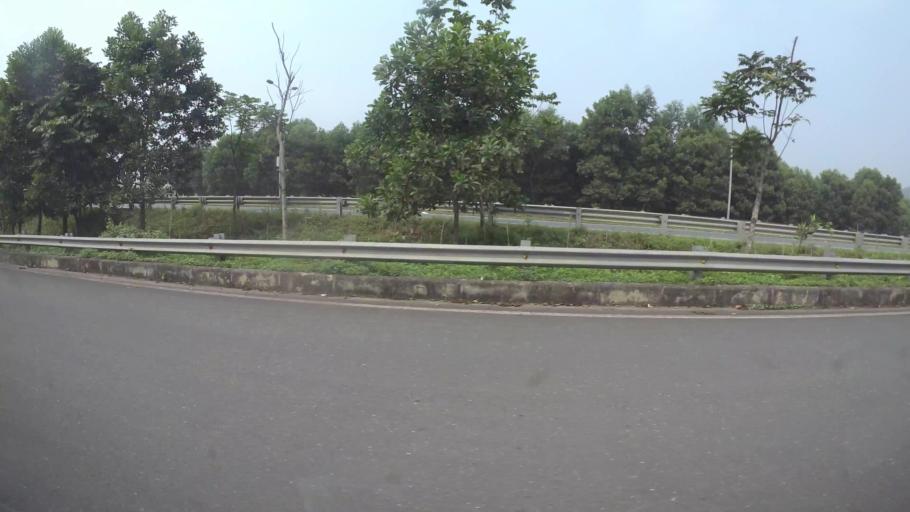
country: VN
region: Ha Noi
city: Lien Quan
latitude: 20.9925
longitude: 105.5274
